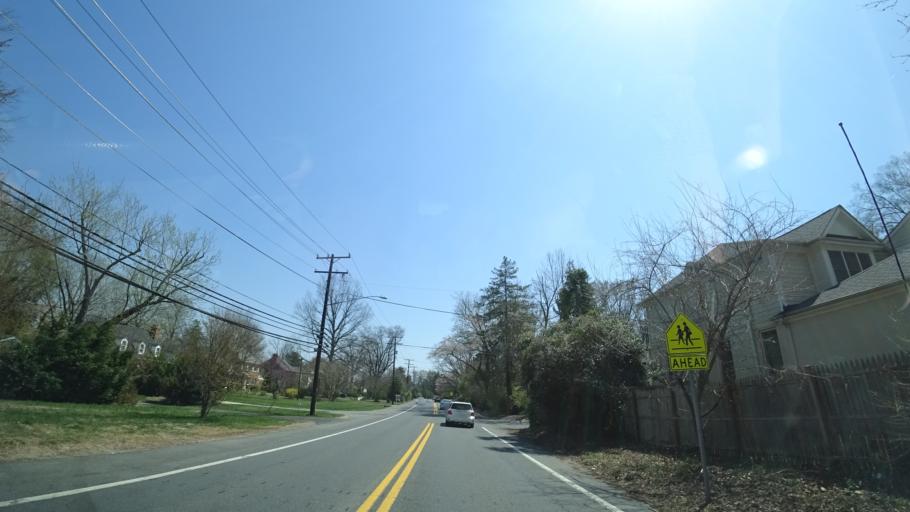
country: US
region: Maryland
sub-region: Montgomery County
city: Bethesda
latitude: 38.9814
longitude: -77.1127
